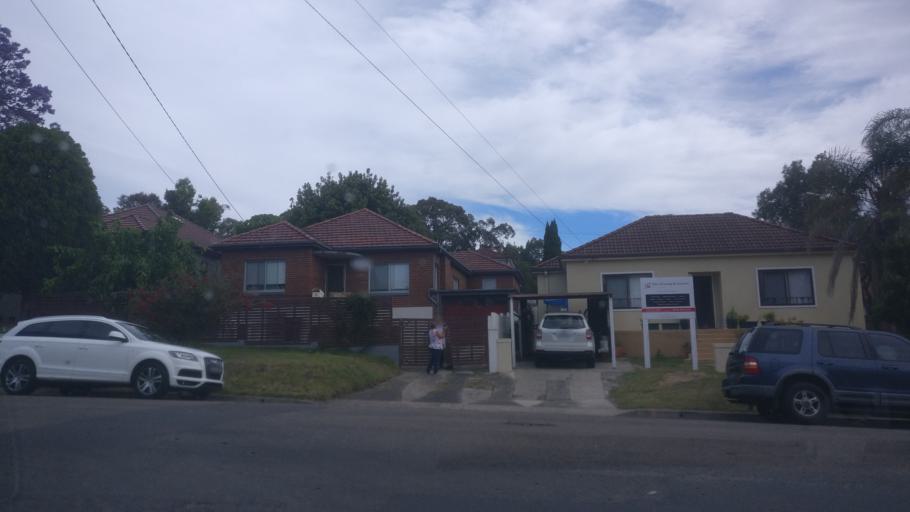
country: AU
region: New South Wales
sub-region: Warringah
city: Brookvale
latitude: -33.7680
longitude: 151.2766
